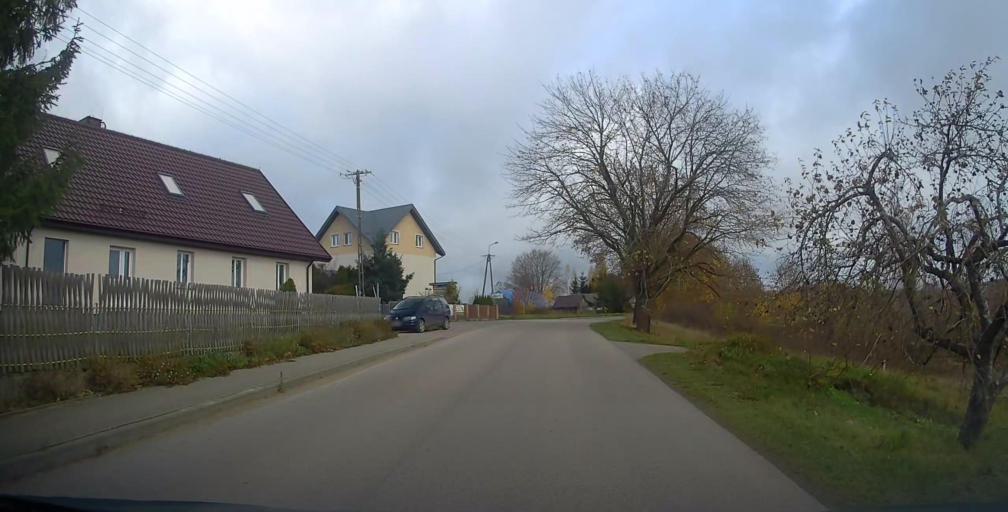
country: PL
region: Podlasie
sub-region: Suwalki
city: Suwalki
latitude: 54.2904
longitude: 22.8796
